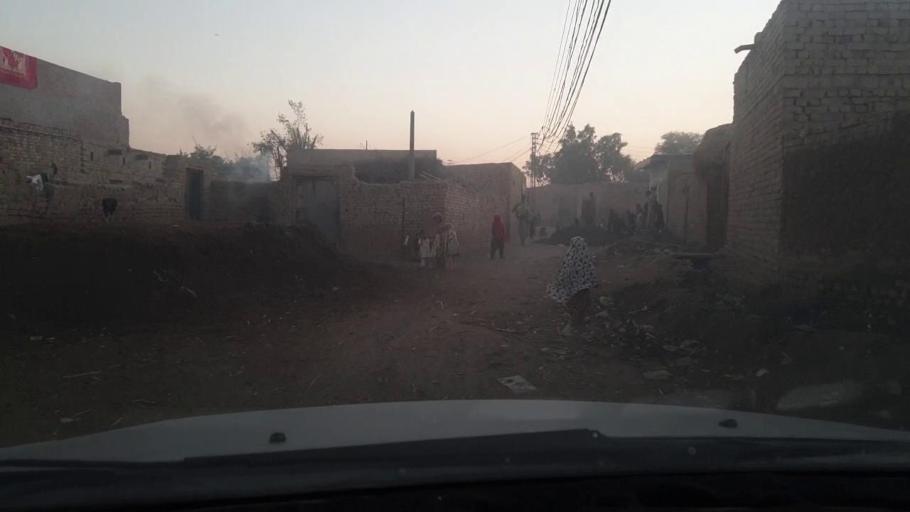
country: PK
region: Sindh
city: Ghotki
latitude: 28.0034
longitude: 69.3373
